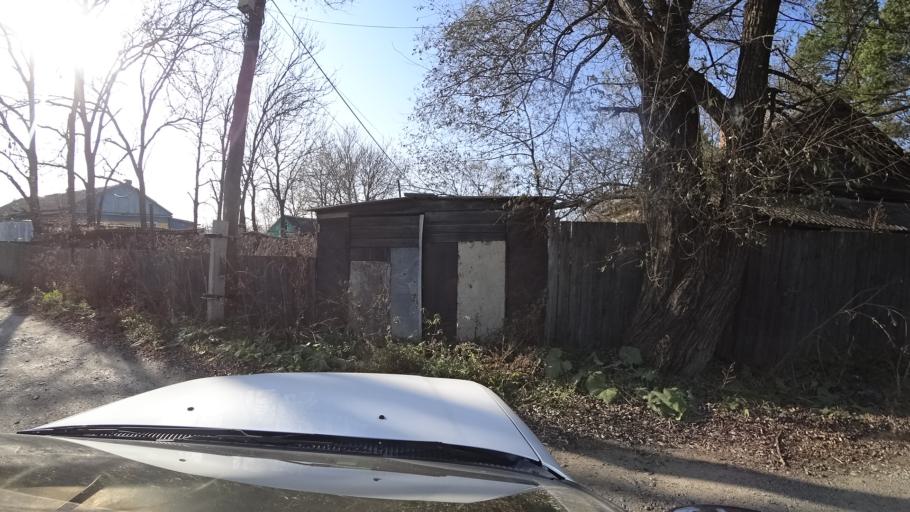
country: RU
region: Primorskiy
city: Dal'nerechensk
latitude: 45.9204
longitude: 133.7537
